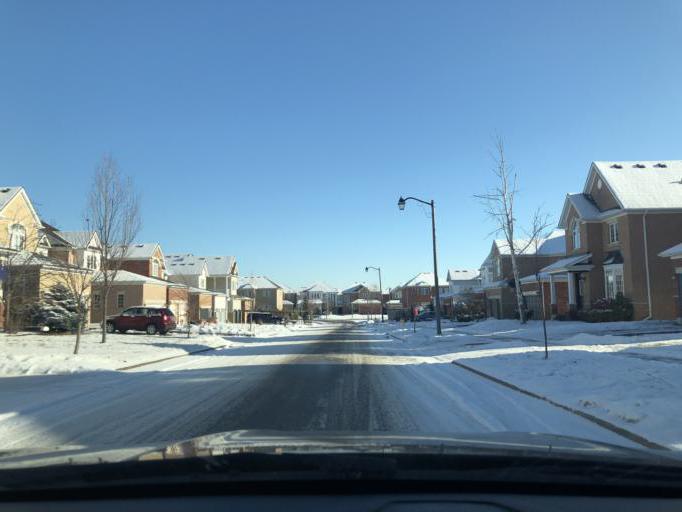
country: CA
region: Ontario
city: Scarborough
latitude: 43.7744
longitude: -79.1409
